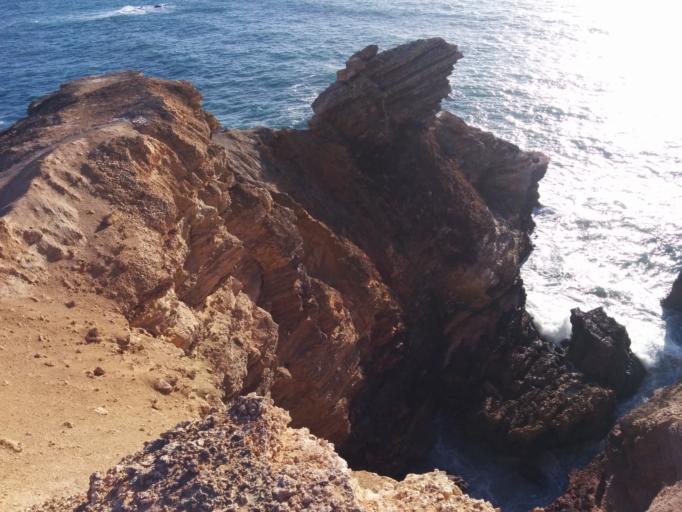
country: PT
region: Faro
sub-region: Vila do Bispo
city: Vila do Bispo
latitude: 37.1906
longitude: -8.9110
